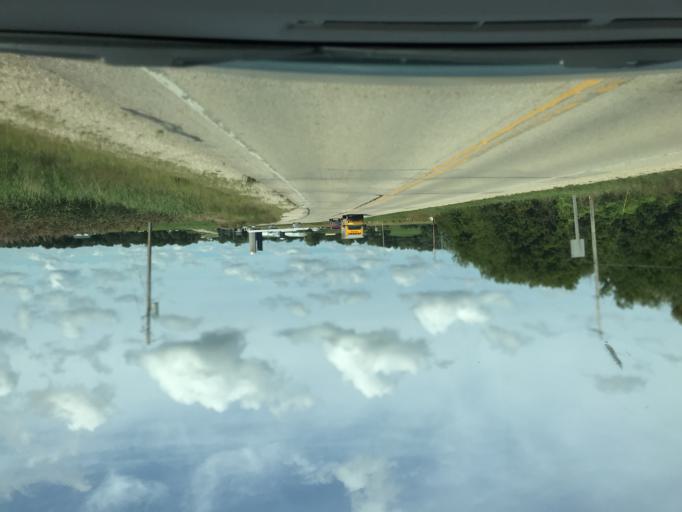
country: US
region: Wisconsin
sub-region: Kenosha County
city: Twin Lakes
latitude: 42.5895
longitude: -88.2213
